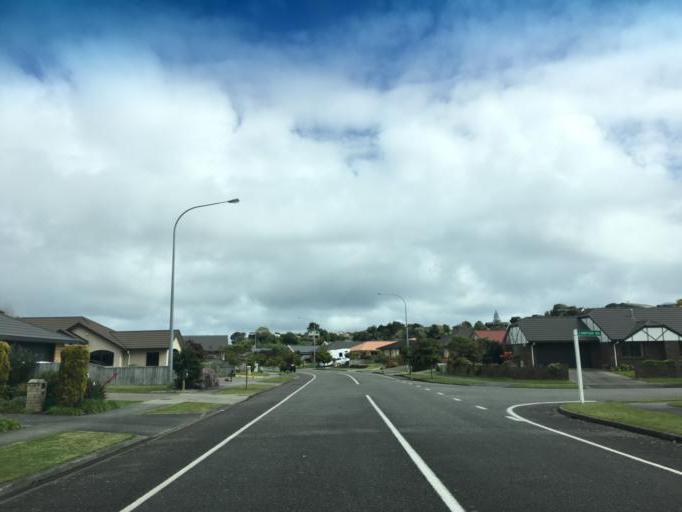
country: NZ
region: Wellington
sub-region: Kapiti Coast District
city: Paraparaumu
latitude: -40.8745
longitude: 175.0208
